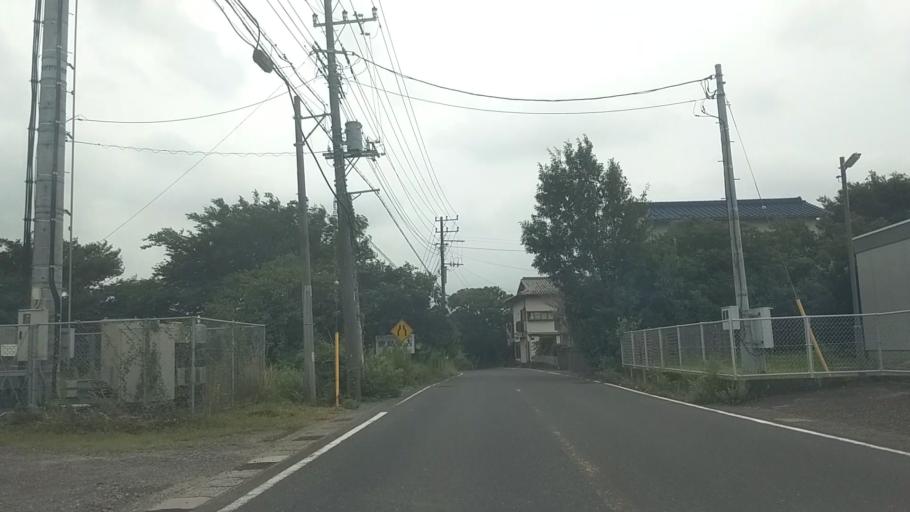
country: JP
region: Chiba
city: Kimitsu
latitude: 35.2168
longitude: 139.9189
